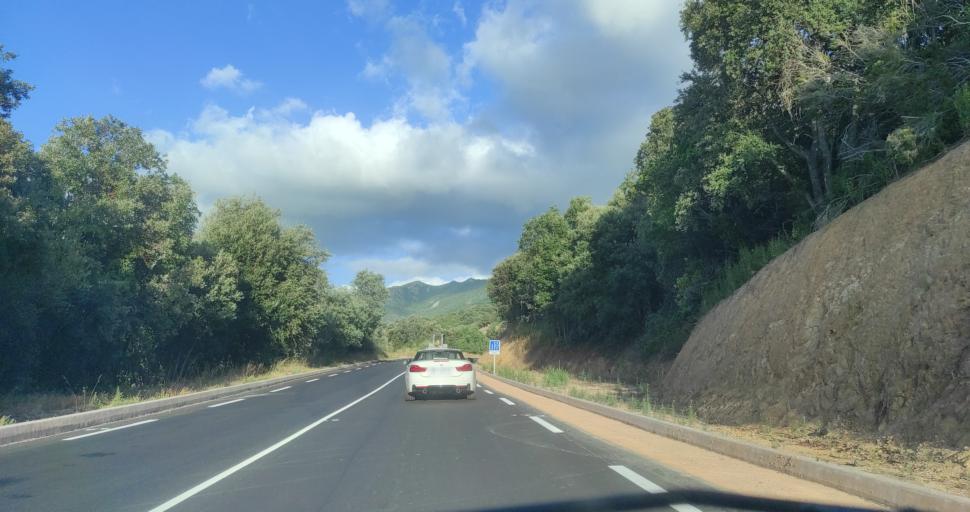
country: FR
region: Corsica
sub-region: Departement de la Corse-du-Sud
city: Appietto
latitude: 42.0358
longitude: 8.7534
